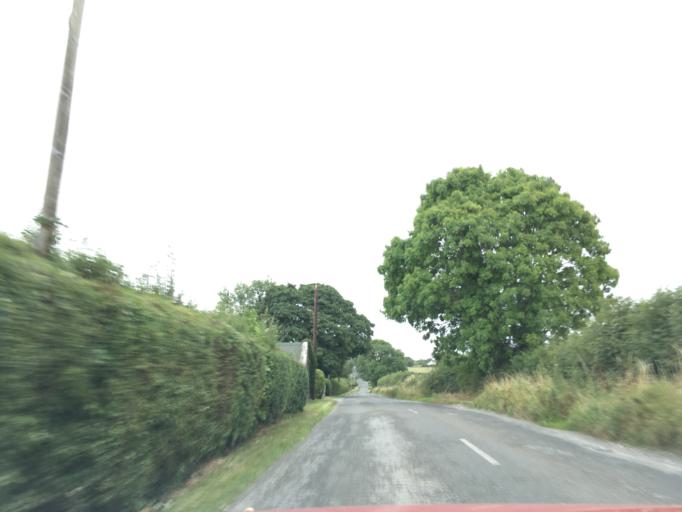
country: IE
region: Munster
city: Cashel
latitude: 52.4748
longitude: -7.8704
